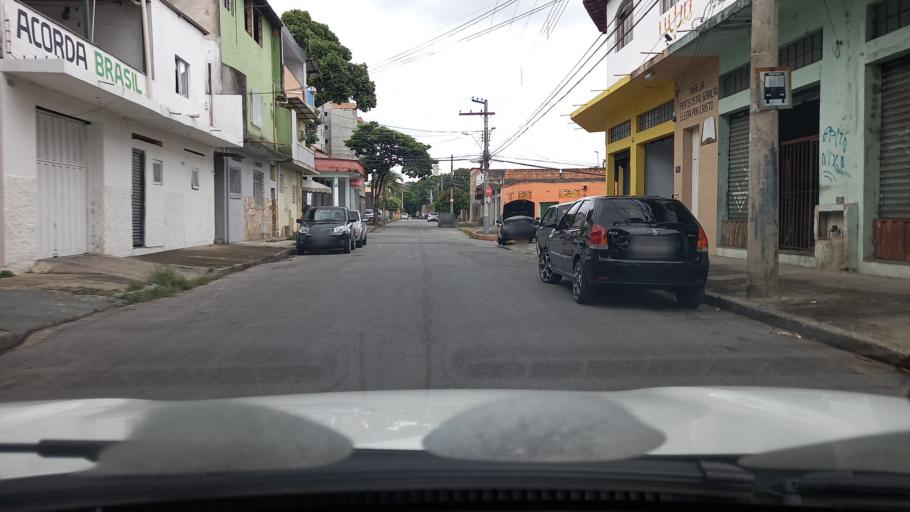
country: BR
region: Minas Gerais
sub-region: Contagem
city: Contagem
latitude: -19.8966
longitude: -44.0132
